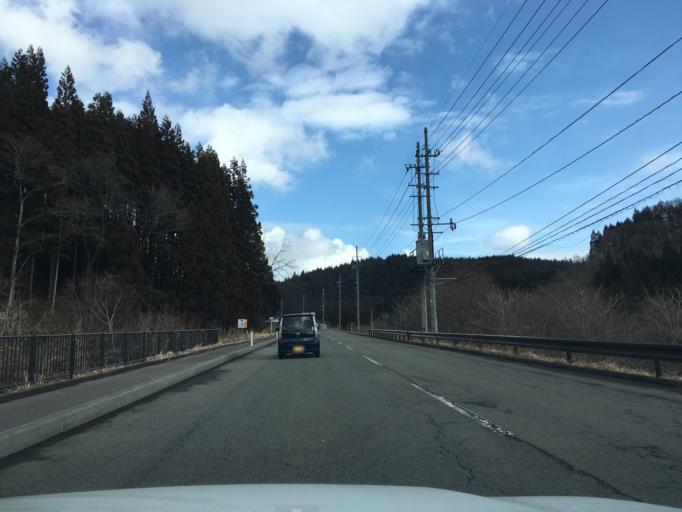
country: JP
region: Akita
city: Takanosu
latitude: 40.0914
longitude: 140.3379
